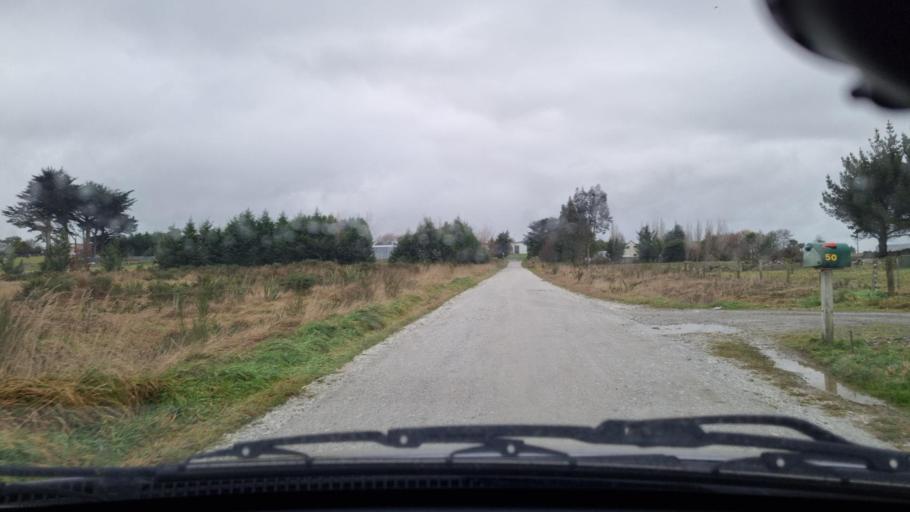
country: NZ
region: Southland
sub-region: Invercargill City
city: Invercargill
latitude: -46.4348
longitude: 168.3897
